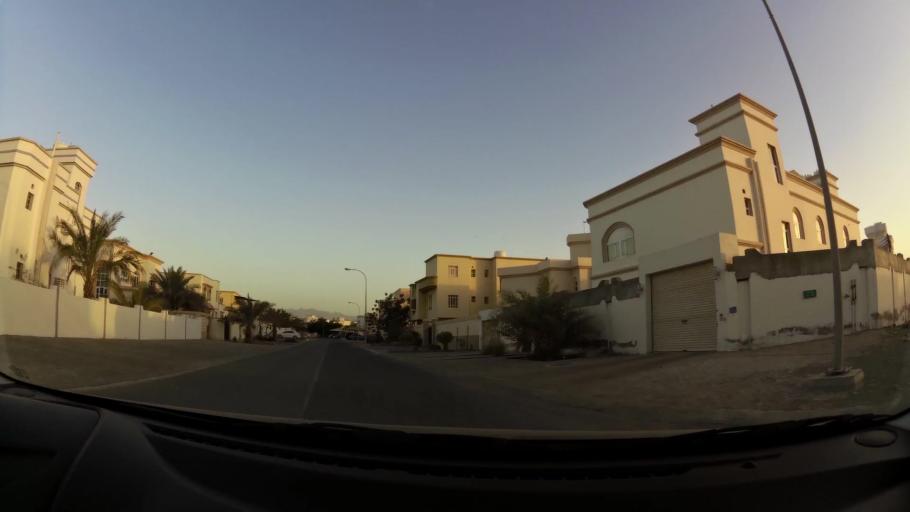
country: OM
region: Muhafazat Masqat
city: As Sib al Jadidah
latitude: 23.5966
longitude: 58.2395
